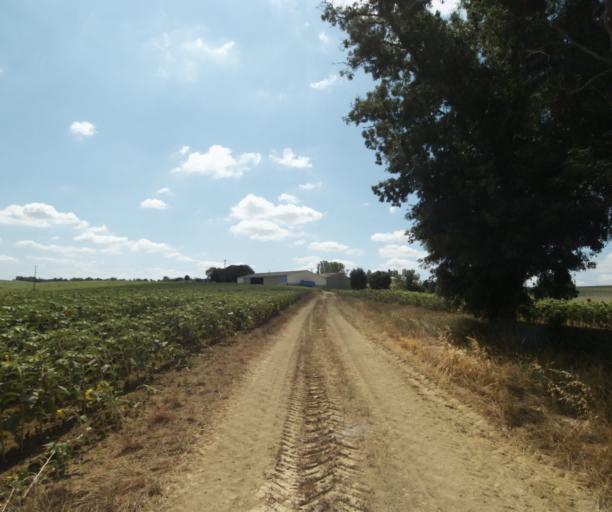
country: FR
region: Midi-Pyrenees
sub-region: Departement de la Haute-Garonne
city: Auriac-sur-Vendinelle
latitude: 43.4693
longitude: 1.8237
